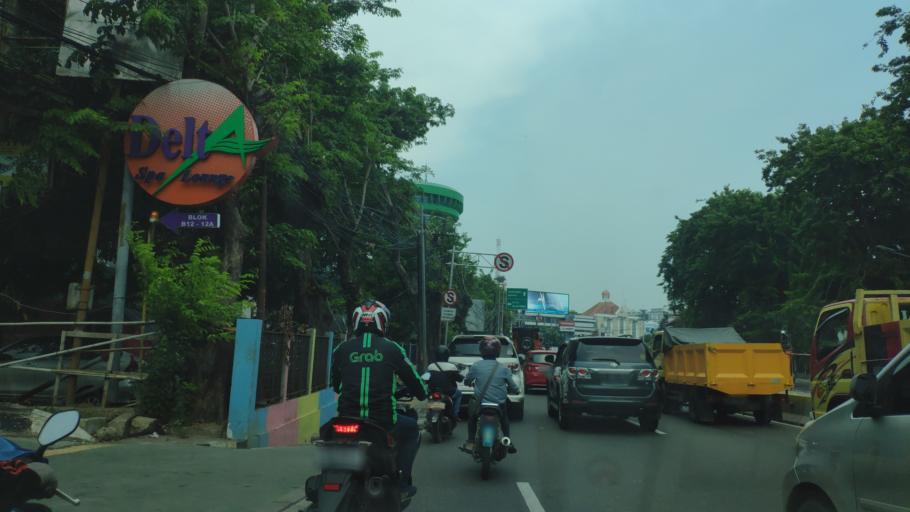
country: ID
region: Jakarta Raya
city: Jakarta
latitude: -6.1689
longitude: 106.8196
